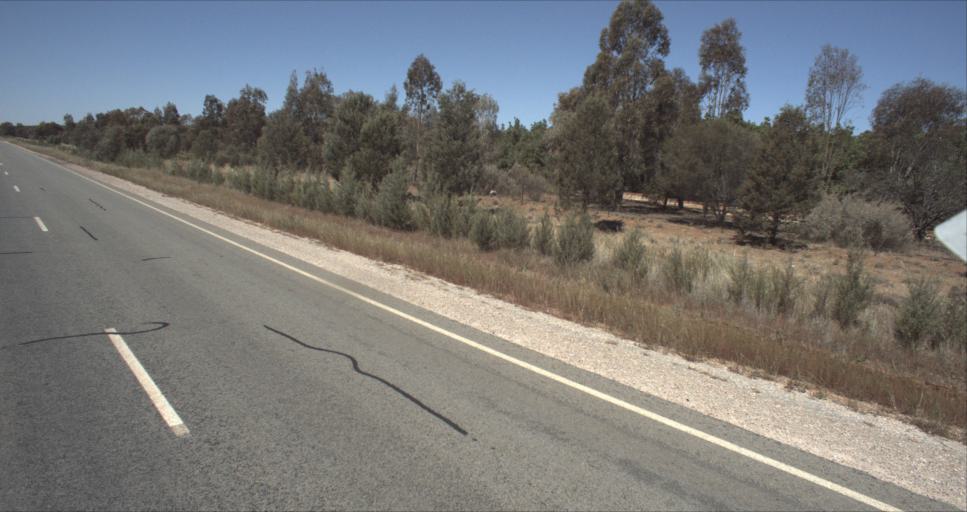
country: AU
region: New South Wales
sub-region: Leeton
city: Leeton
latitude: -34.5018
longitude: 146.4464
